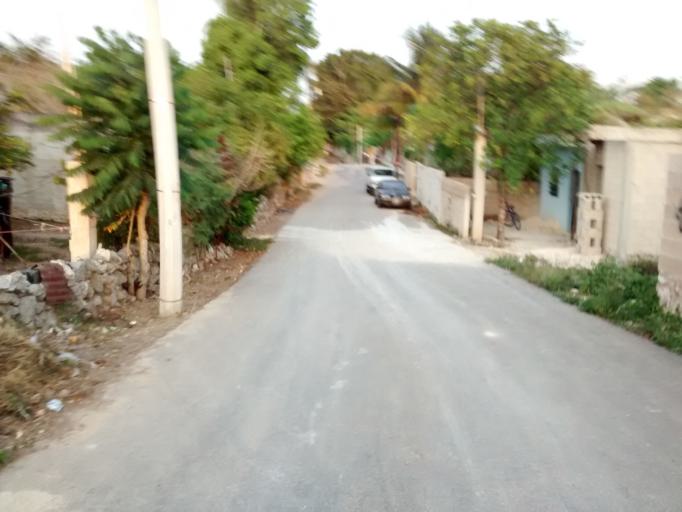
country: MX
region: Yucatan
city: Valladolid
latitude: 20.6813
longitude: -88.1869
